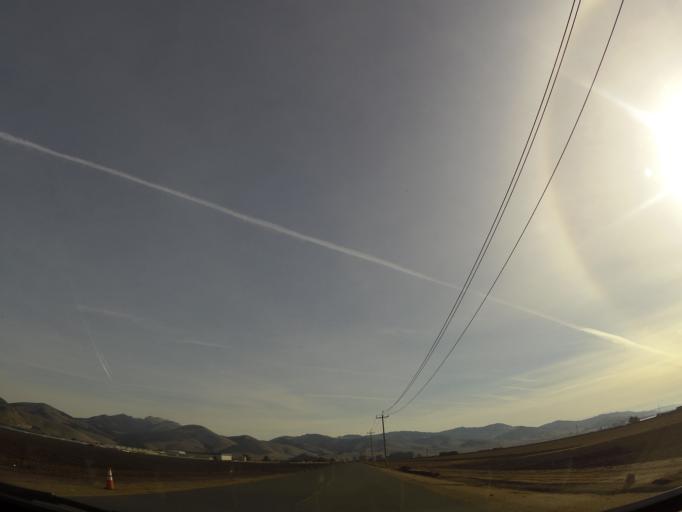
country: US
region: California
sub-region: Monterey County
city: Boronda
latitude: 36.7290
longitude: -121.6236
